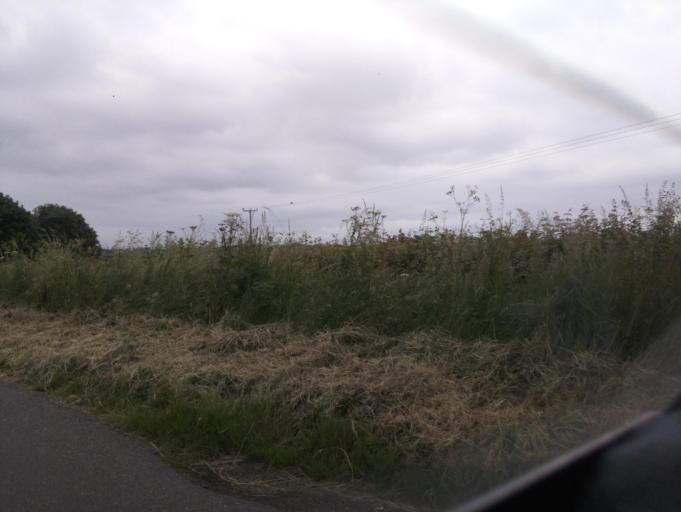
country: GB
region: England
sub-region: Leicestershire
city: Melton Mowbray
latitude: 52.7166
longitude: -0.8296
